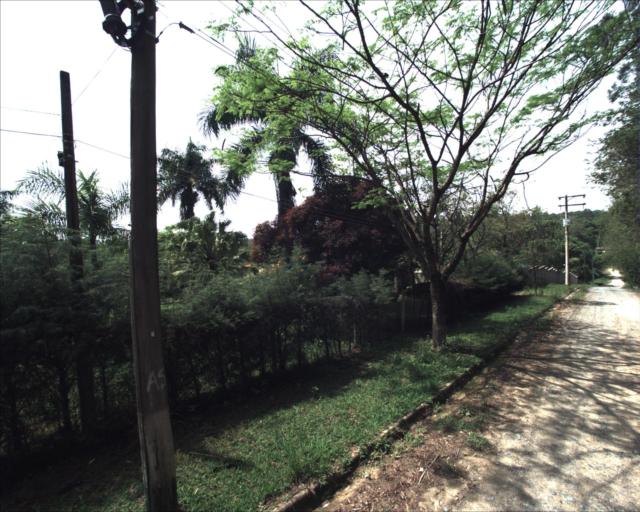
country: BR
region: Sao Paulo
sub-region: Aracoiaba Da Serra
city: Aracoiaba da Serra
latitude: -23.5607
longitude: -47.5365
